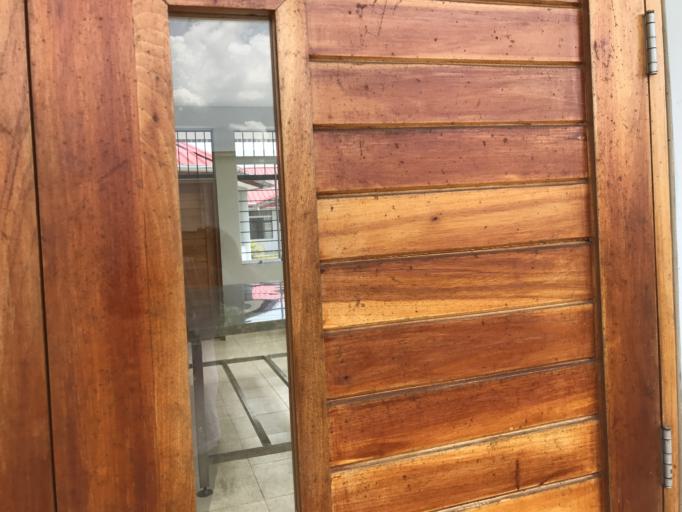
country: PE
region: Loreto
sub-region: Provincia de Maynas
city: Iquitos
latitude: -3.7989
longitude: -73.3071
